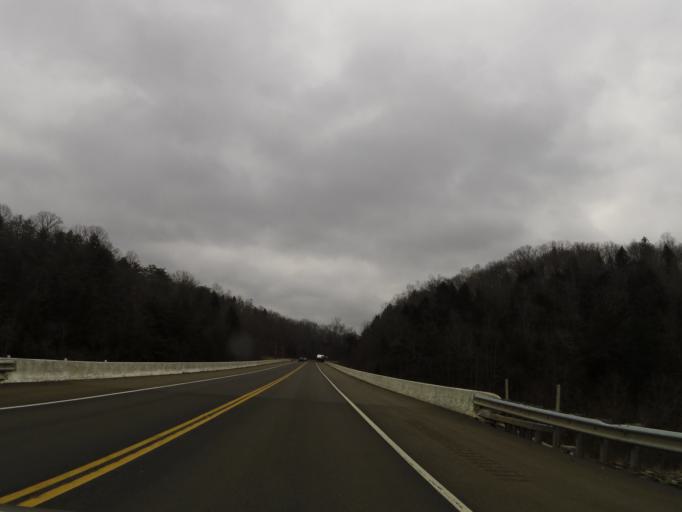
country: US
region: Tennessee
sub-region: Scott County
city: Huntsville
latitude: 36.3825
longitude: -84.4152
